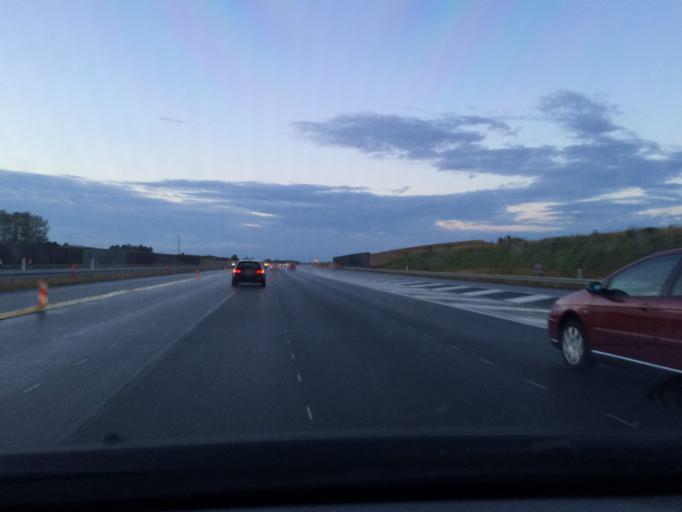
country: DK
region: Zealand
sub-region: Solrod Kommune
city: Solrod Strand
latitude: 55.5619
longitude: 12.2315
